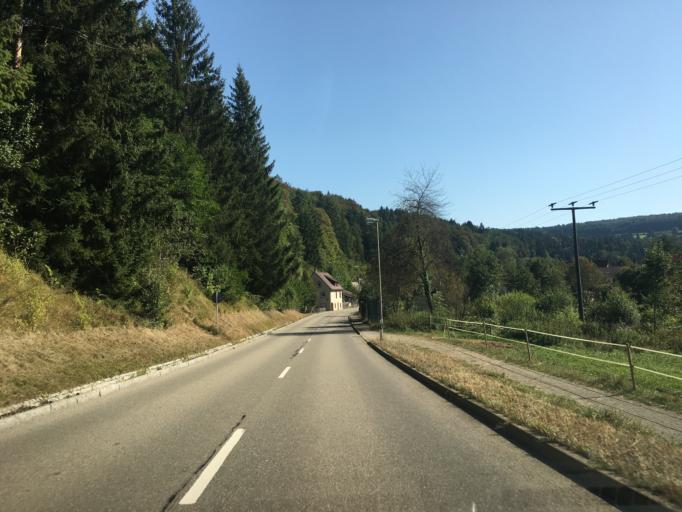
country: DE
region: Baden-Wuerttemberg
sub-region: Tuebingen Region
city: Hayingen
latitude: 48.3218
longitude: 9.5049
